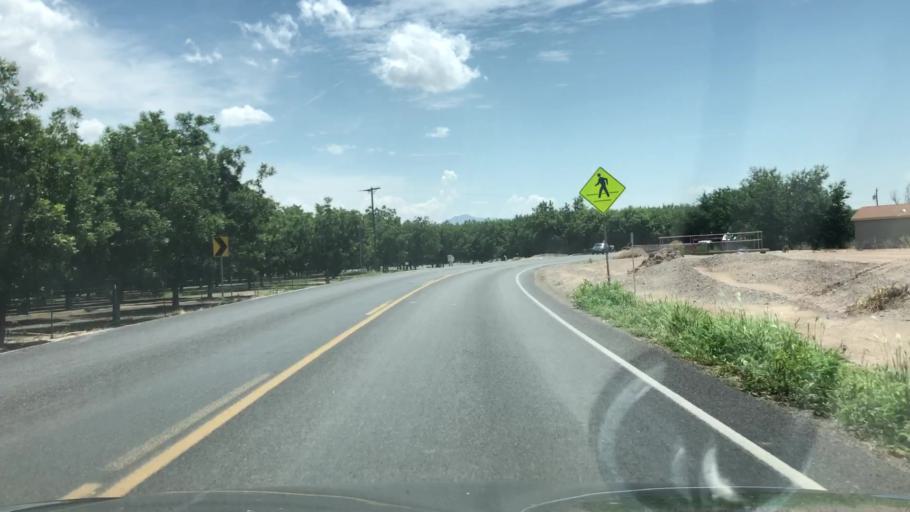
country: US
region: New Mexico
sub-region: Dona Ana County
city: Anthony
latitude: 32.0029
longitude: -106.6580
